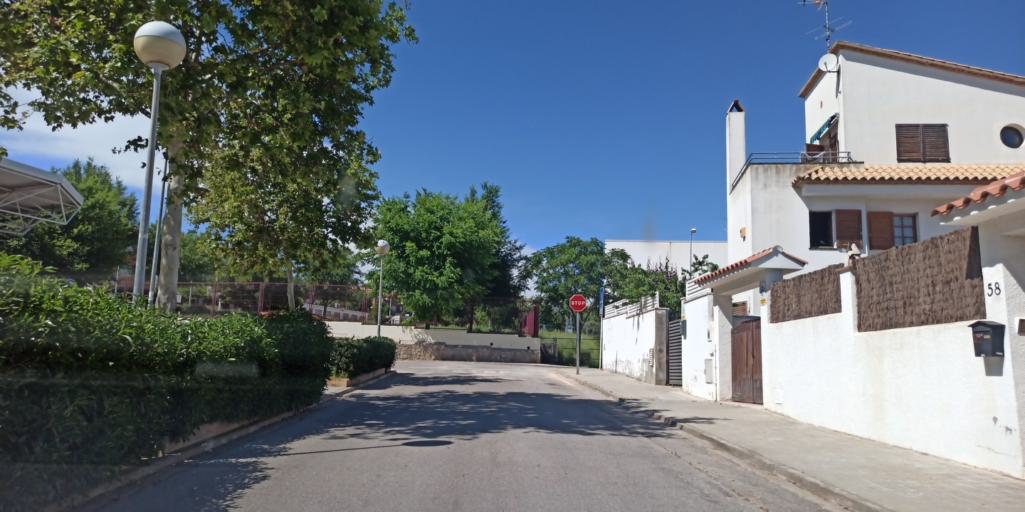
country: ES
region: Catalonia
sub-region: Provincia de Barcelona
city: Sant Pere de Ribes
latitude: 41.2601
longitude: 1.7808
